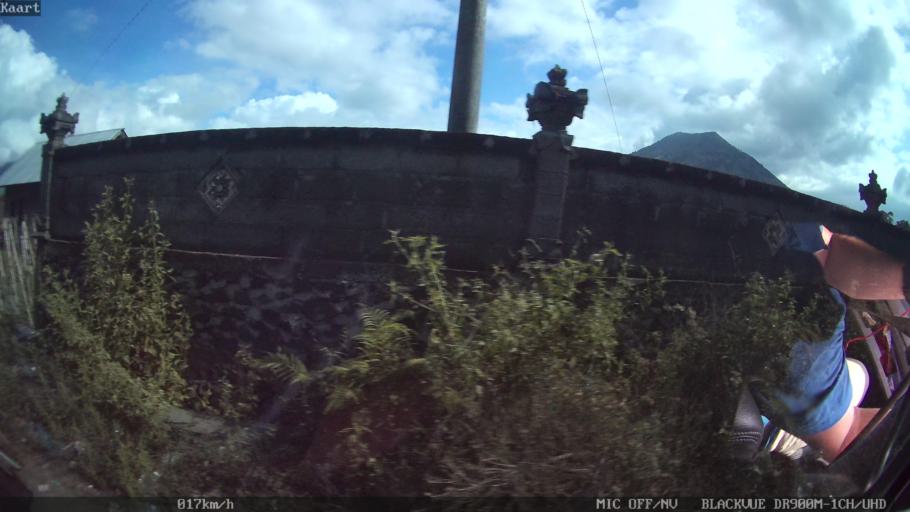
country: ID
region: Bali
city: Banjar Trunyan
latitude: -8.2244
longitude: 115.3976
